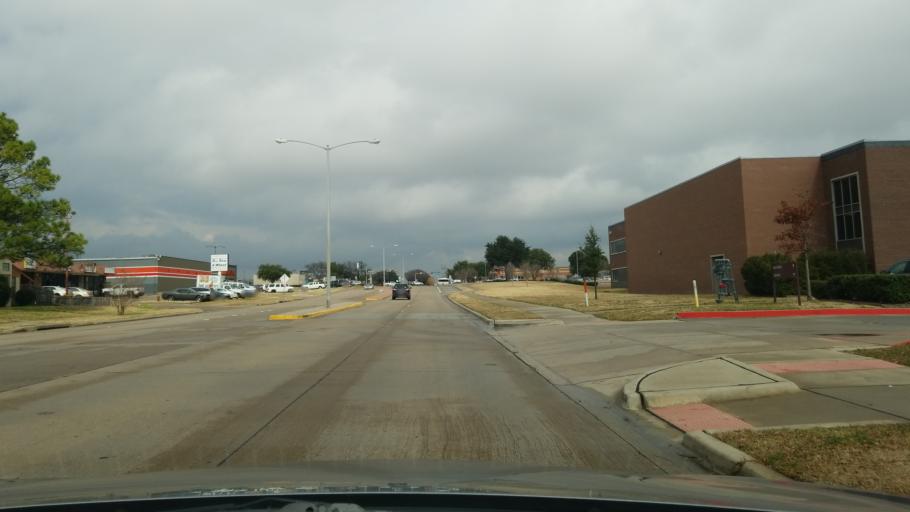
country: US
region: Texas
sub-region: Denton County
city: Lewisville
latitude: 33.0394
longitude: -97.0205
